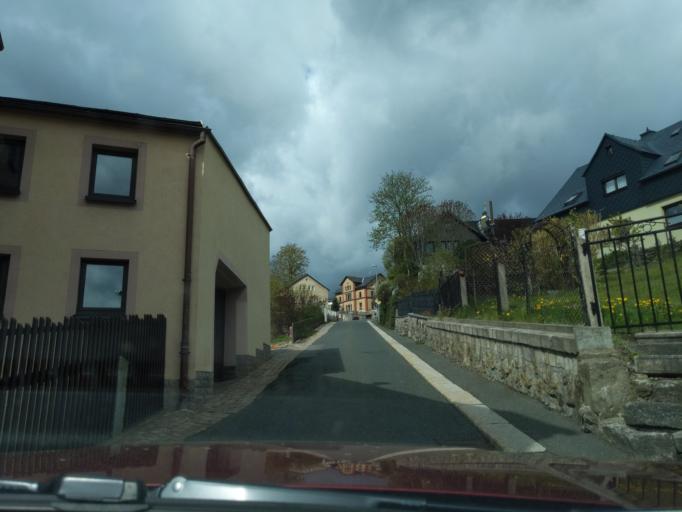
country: DE
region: Saxony
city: Schoenheide
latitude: 50.5042
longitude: 12.5376
